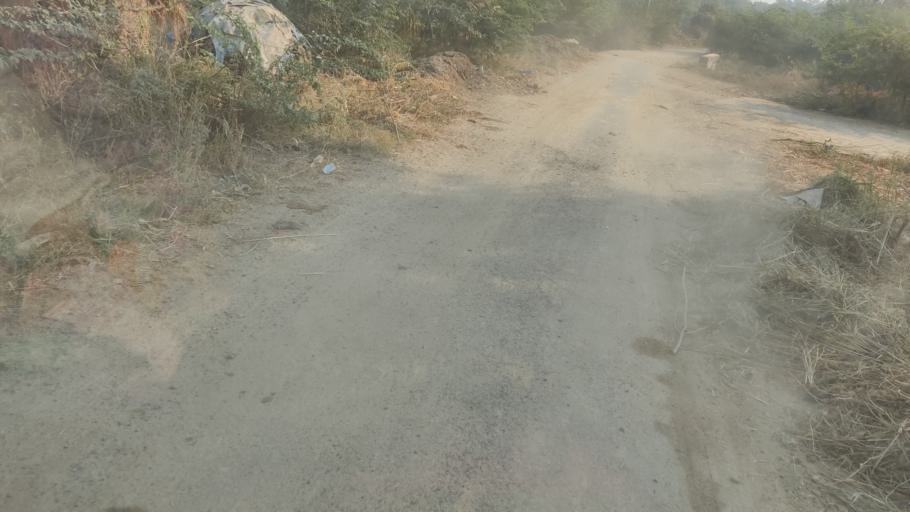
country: IN
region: Uttar Pradesh
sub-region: Mathura
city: Mathura
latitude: 27.5412
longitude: 77.6009
